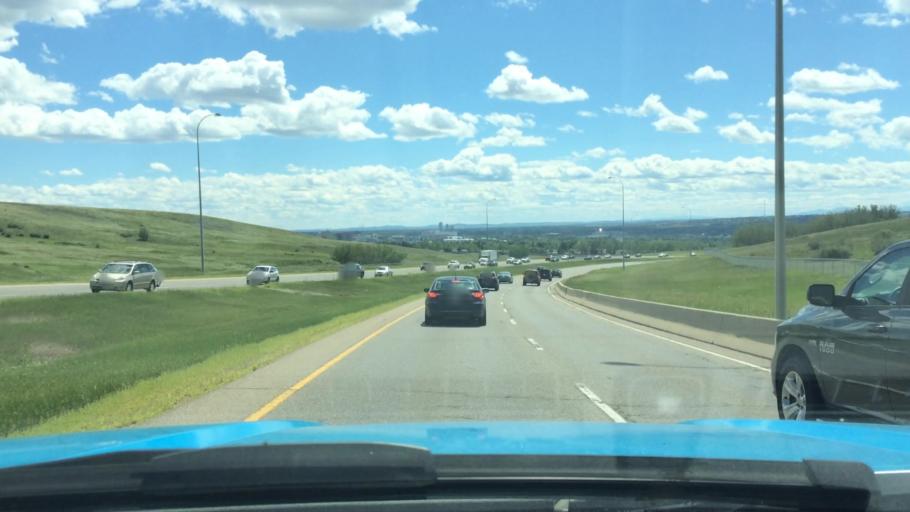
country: CA
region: Alberta
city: Calgary
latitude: 51.1172
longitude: -114.1342
